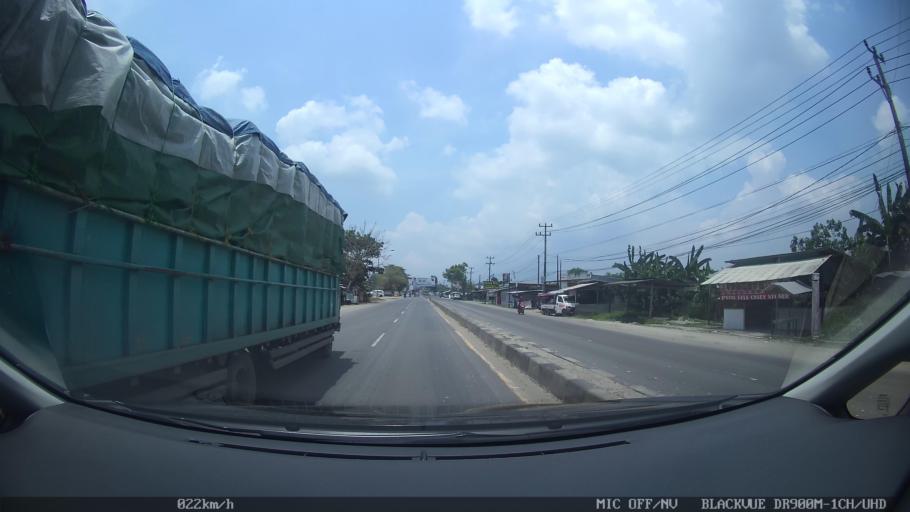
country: ID
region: Lampung
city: Natar
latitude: -5.2988
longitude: 105.1920
